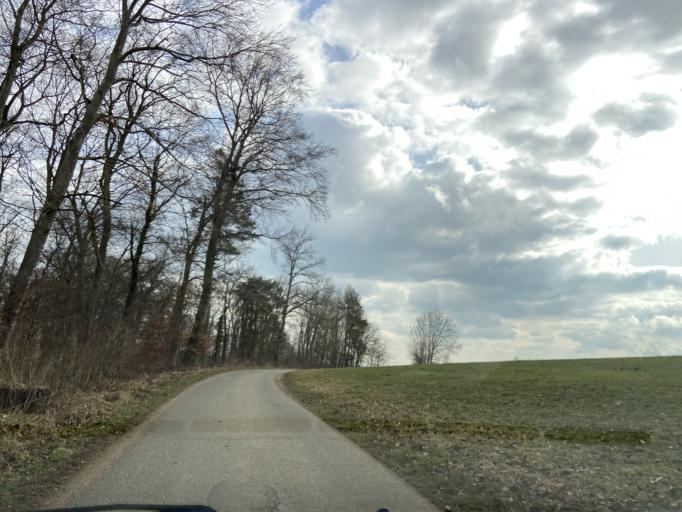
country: DE
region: Baden-Wuerttemberg
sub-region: Tuebingen Region
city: Bingen
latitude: 48.1169
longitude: 9.2593
